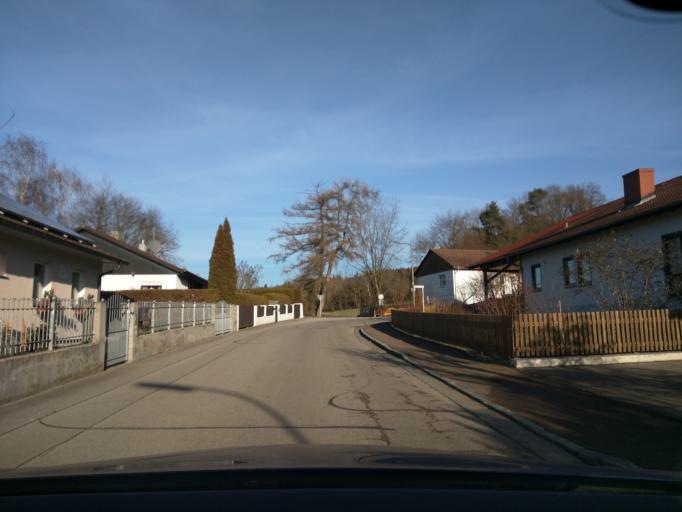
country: DE
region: Bavaria
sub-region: Upper Bavaria
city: Au in der Hallertau
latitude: 48.5623
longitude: 11.7419
